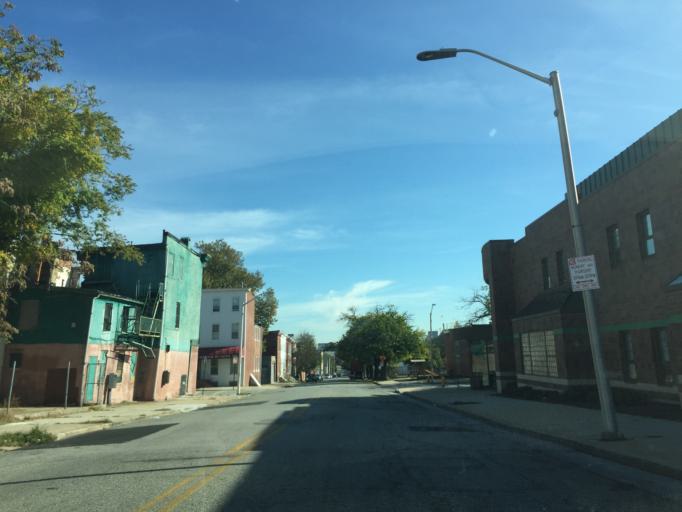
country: US
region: Maryland
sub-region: City of Baltimore
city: Baltimore
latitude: 39.2921
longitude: -76.6418
